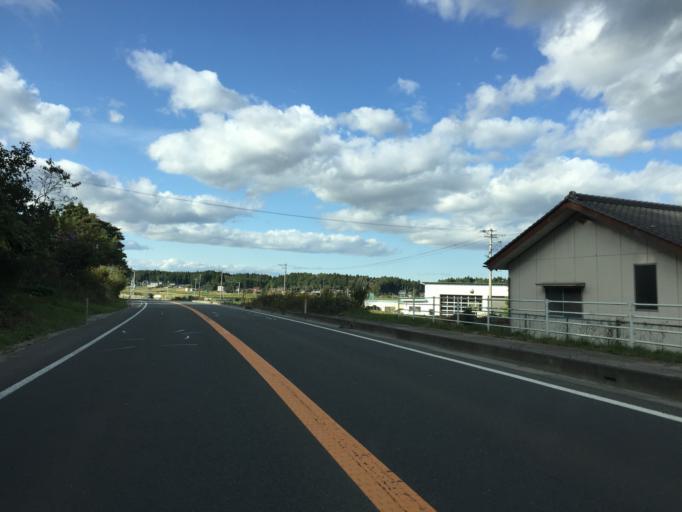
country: JP
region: Miyagi
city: Marumori
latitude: 37.8876
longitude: 140.9128
